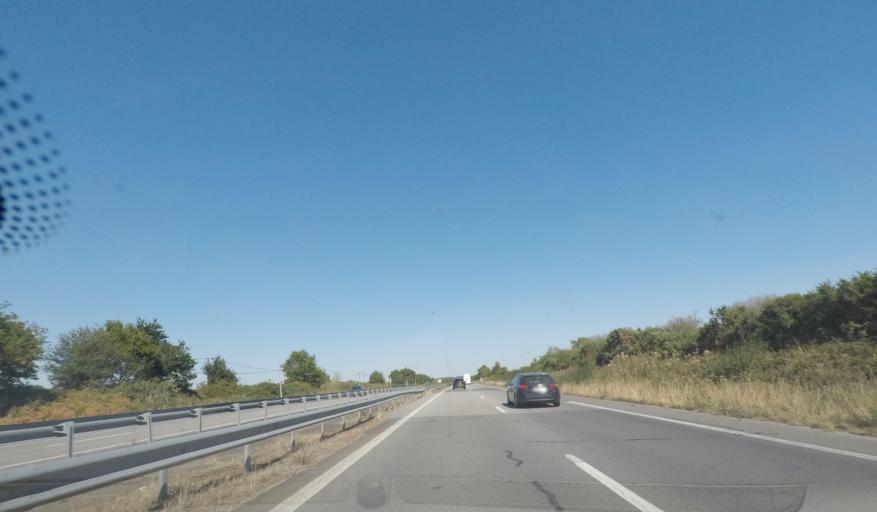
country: FR
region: Brittany
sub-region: Departement du Morbihan
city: Peaule
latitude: 47.5374
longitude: -2.3875
